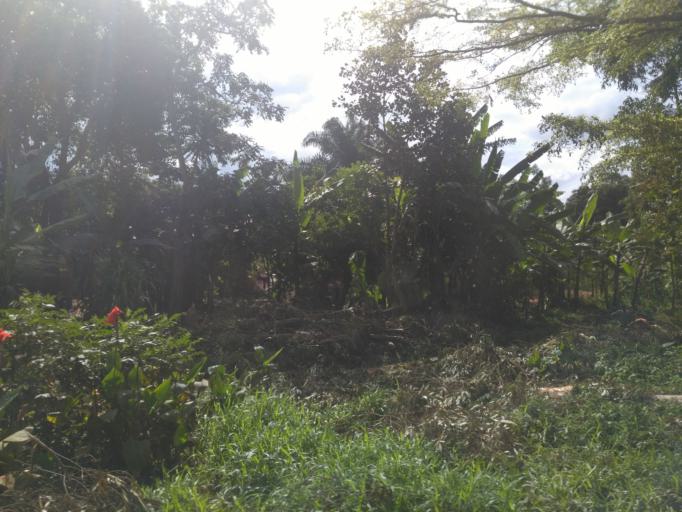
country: UG
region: Central Region
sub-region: Buikwe District
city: Njeru
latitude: 0.3948
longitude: 33.1729
